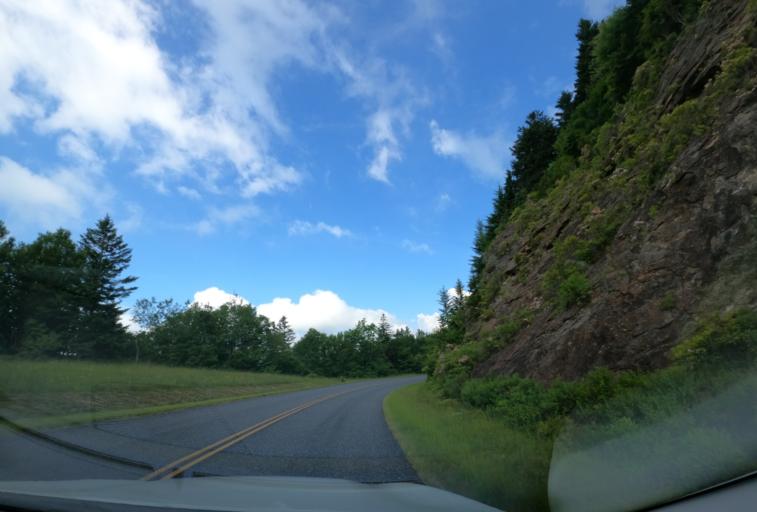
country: US
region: North Carolina
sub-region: Haywood County
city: Hazelwood
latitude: 35.3732
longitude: -83.0022
